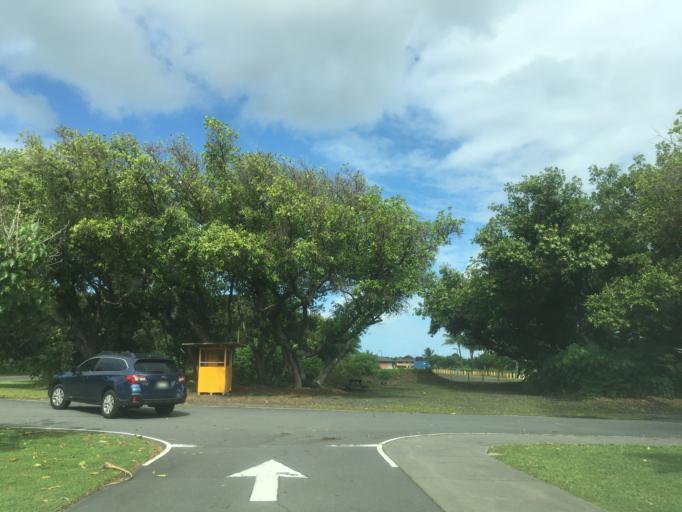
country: US
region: Hawaii
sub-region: Hawaii County
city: Leilani Estates
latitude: 19.4582
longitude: -154.8415
